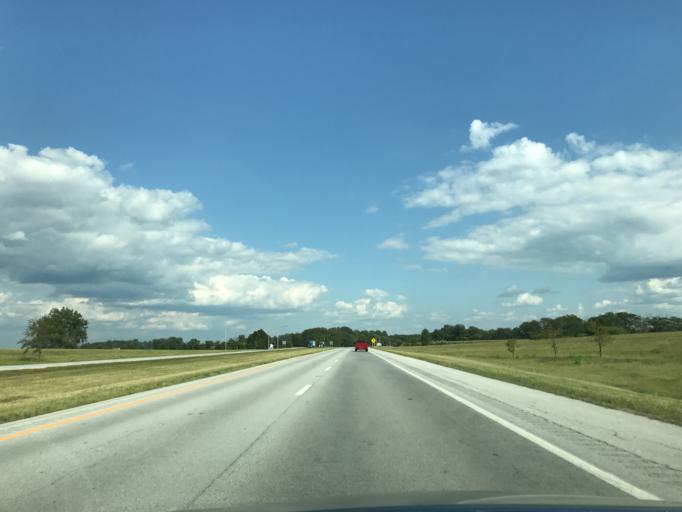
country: US
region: Ohio
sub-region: Allen County
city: Delphos
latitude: 40.8732
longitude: -84.3503
